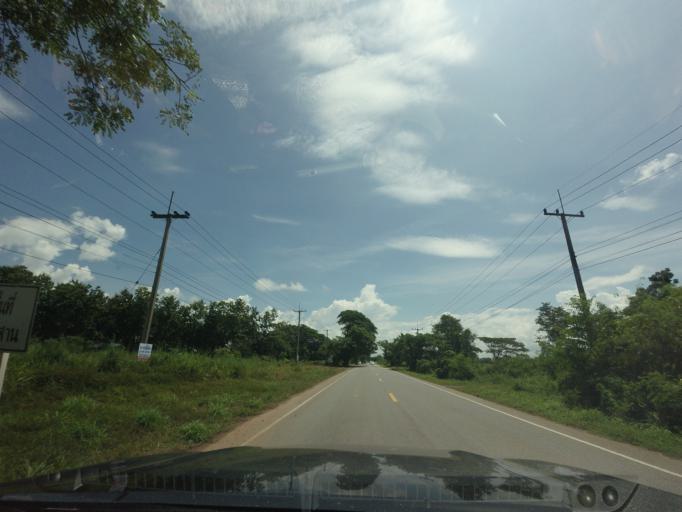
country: TH
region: Changwat Udon Thani
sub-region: Amphoe Ban Phue
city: Ban Phue
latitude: 17.7183
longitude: 102.4016
